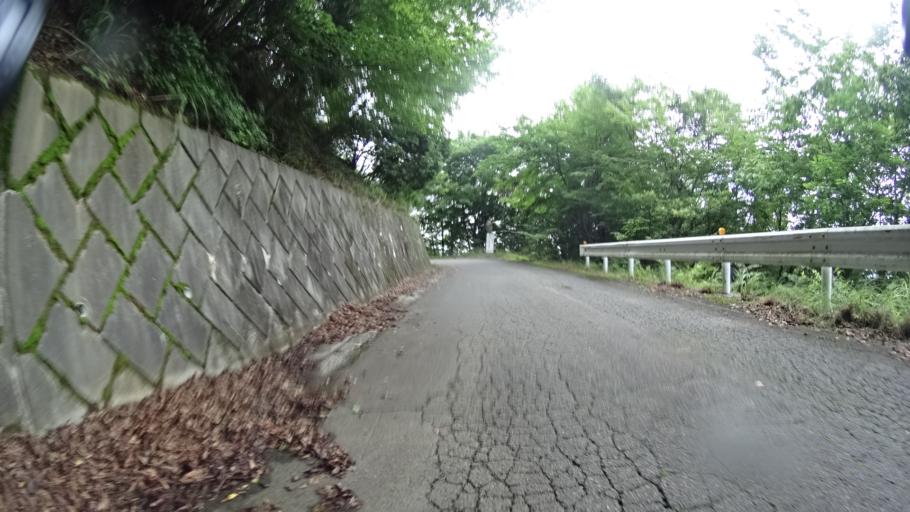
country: JP
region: Saitama
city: Chichibu
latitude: 35.8854
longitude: 139.1192
